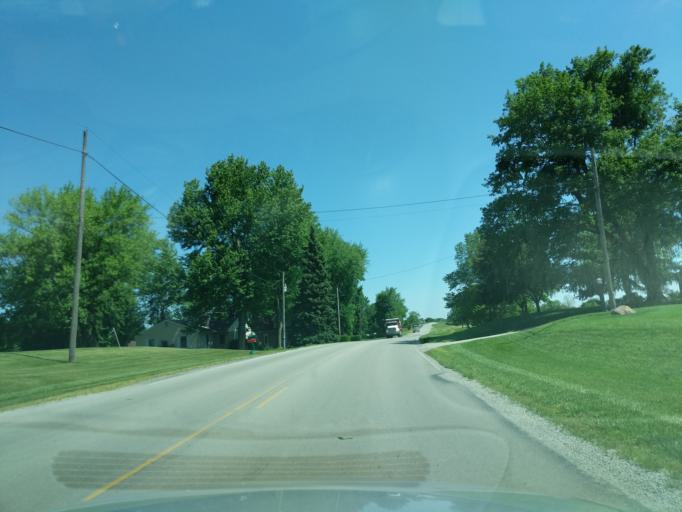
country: US
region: Indiana
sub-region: Huntington County
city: Huntington
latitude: 40.8976
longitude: -85.4844
